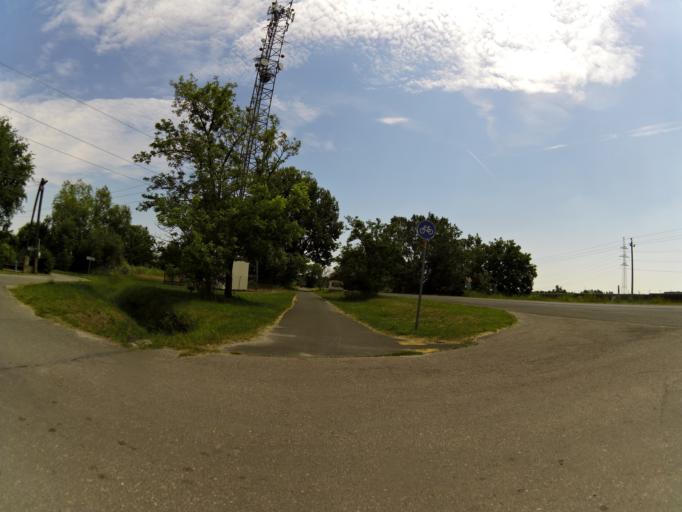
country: HU
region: Csongrad
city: Kistelek
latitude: 46.4598
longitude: 19.9883
